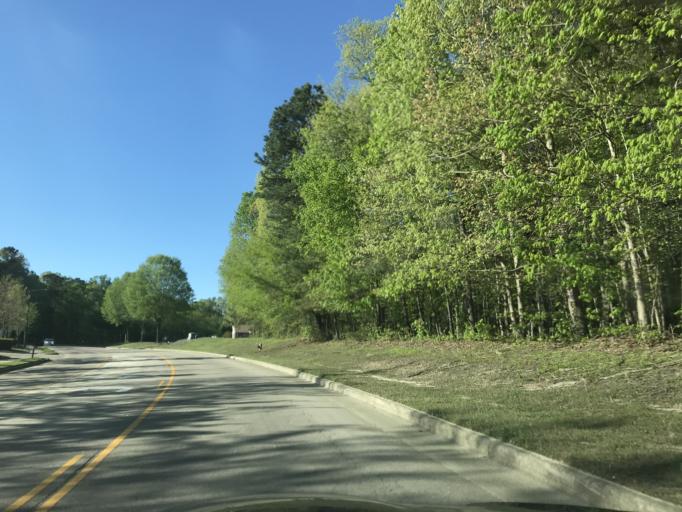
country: US
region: North Carolina
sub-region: Wake County
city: Knightdale
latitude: 35.8008
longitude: -78.5564
